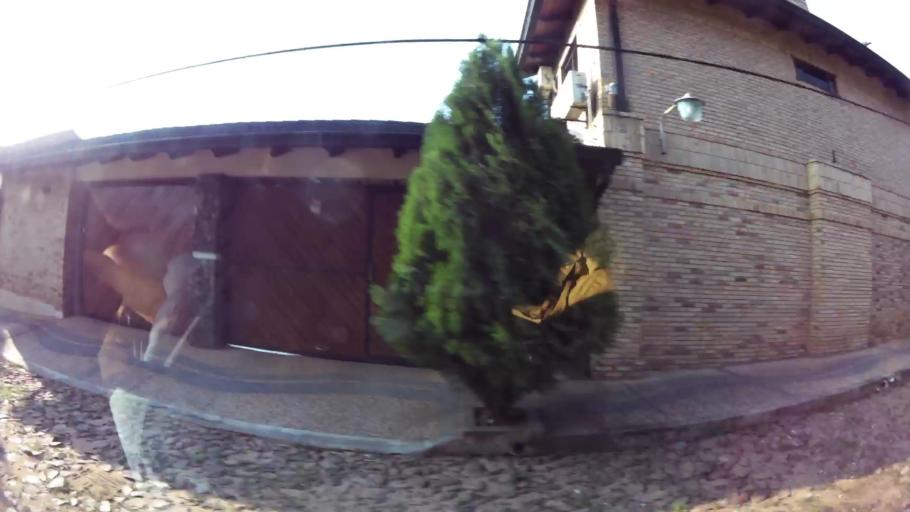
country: PY
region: Central
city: Lambare
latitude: -25.3426
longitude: -57.6001
